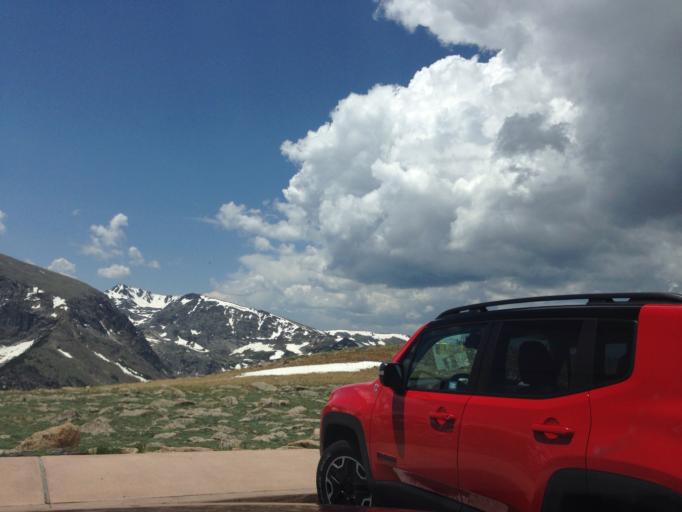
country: US
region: Colorado
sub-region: Larimer County
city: Estes Park
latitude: 40.3954
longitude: -105.7114
